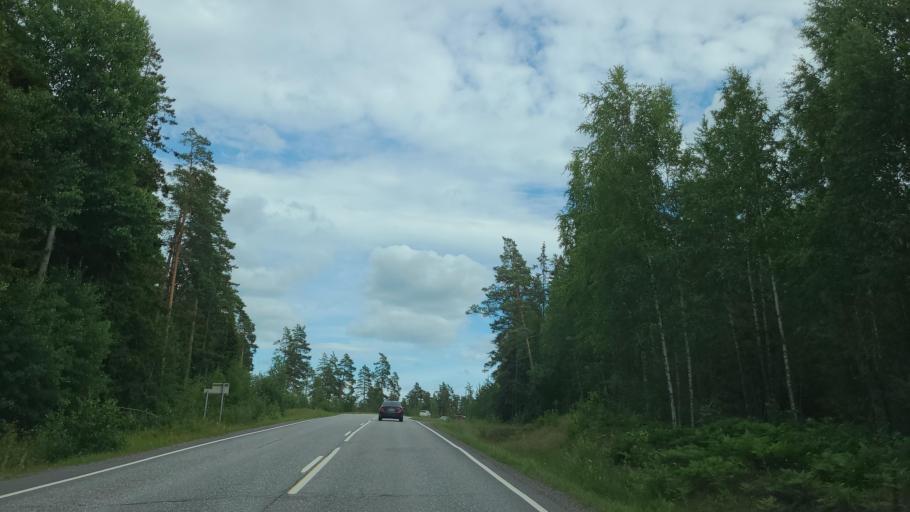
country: FI
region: Varsinais-Suomi
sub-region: Turku
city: Rymaettylae
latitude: 60.3906
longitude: 21.9102
